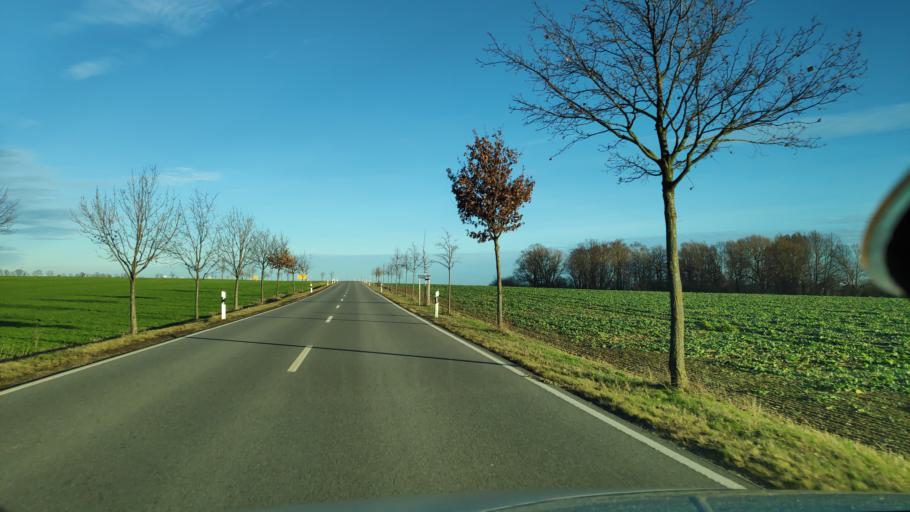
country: DE
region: Thuringia
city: Seelingstadt
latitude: 50.7987
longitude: 12.2561
